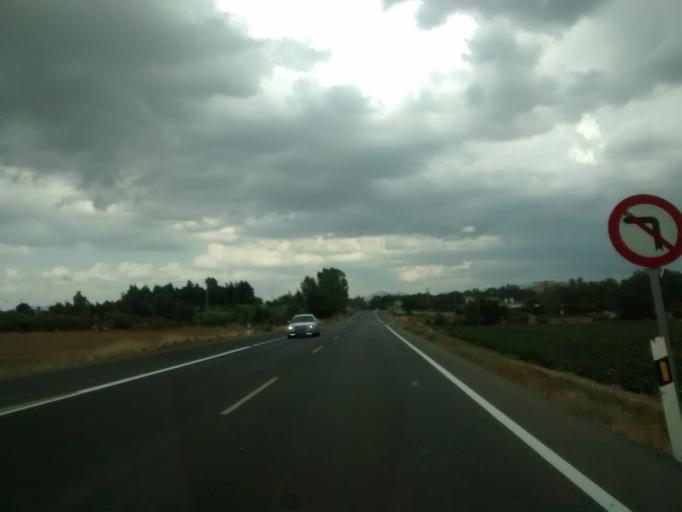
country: ES
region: Andalusia
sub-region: Provincia de Cadiz
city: Villamartin
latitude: 36.8438
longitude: -5.6911
